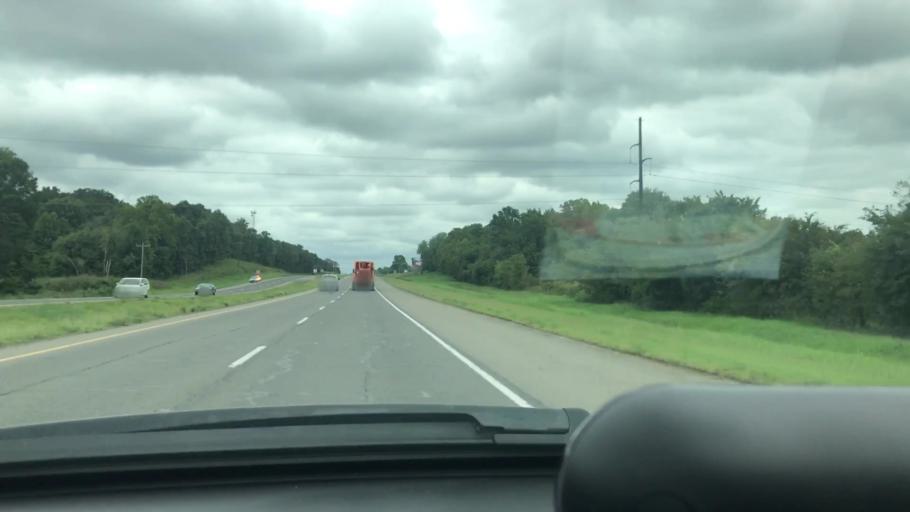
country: US
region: Oklahoma
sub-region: Muskogee County
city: Muskogee
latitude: 35.8197
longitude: -95.4026
